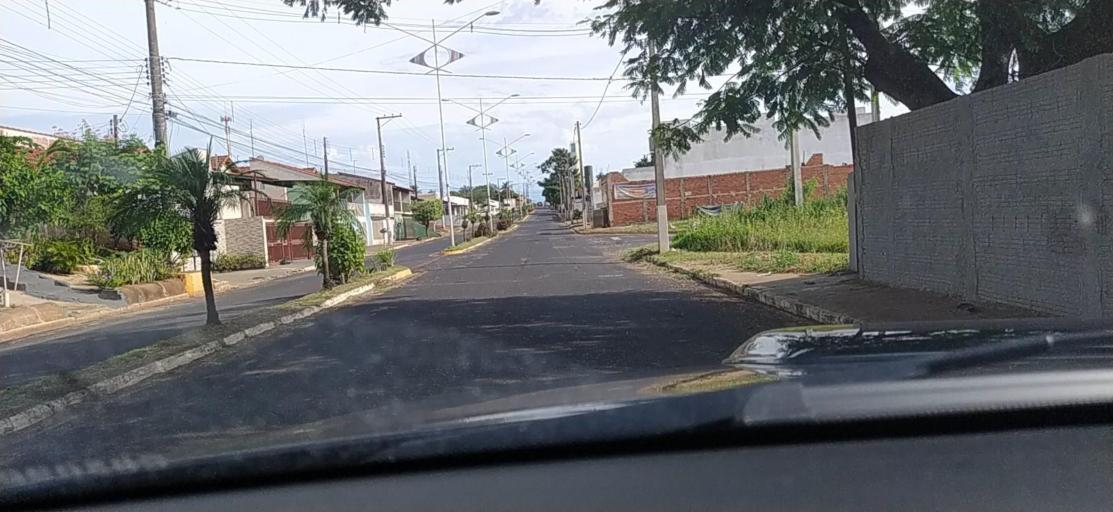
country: BR
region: Sao Paulo
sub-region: Catanduva
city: Catanduva
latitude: -21.0629
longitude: -49.0627
